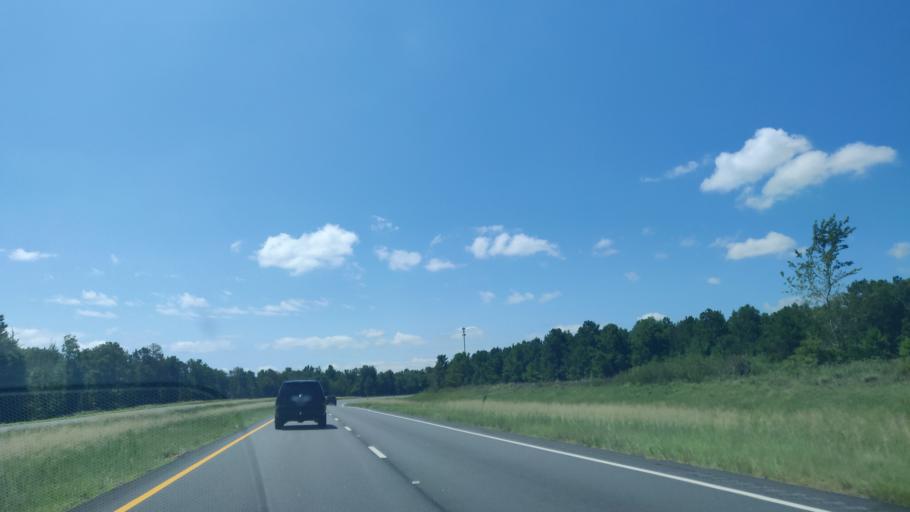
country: US
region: Georgia
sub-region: Stewart County
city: Richland
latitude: 32.1960
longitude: -84.6999
